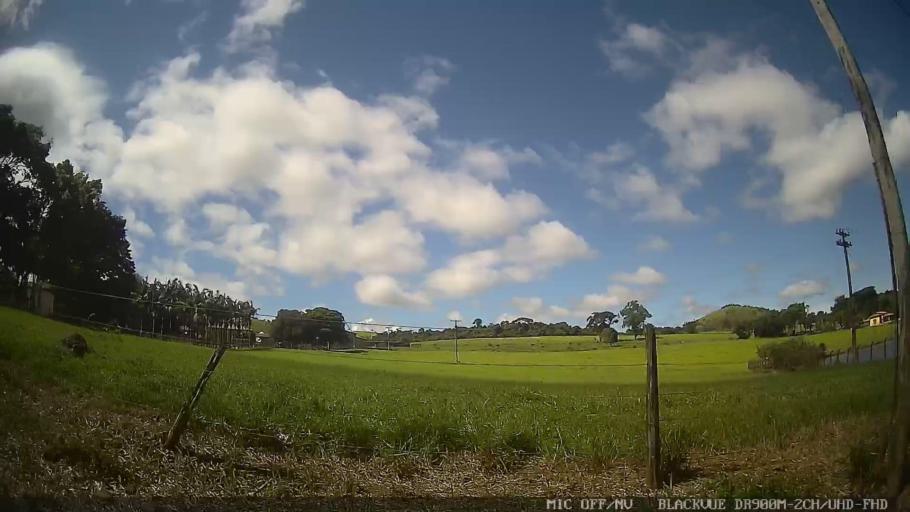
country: BR
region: Sao Paulo
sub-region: Amparo
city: Amparo
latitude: -22.8563
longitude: -46.7722
